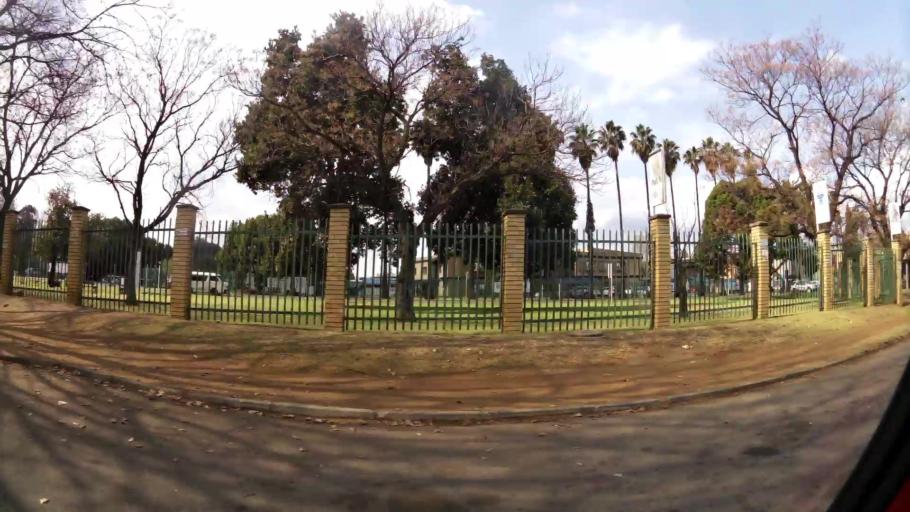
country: ZA
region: Gauteng
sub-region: Sedibeng District Municipality
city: Vanderbijlpark
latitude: -26.7098
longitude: 27.8603
